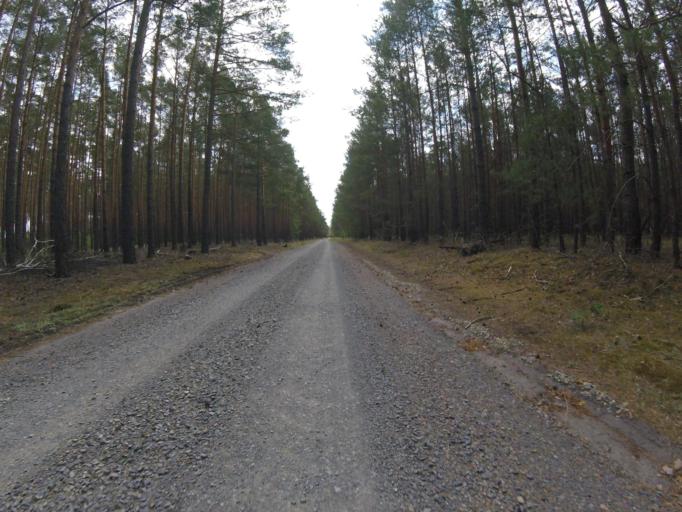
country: DE
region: Brandenburg
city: Gross Koris
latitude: 52.1363
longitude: 13.6612
